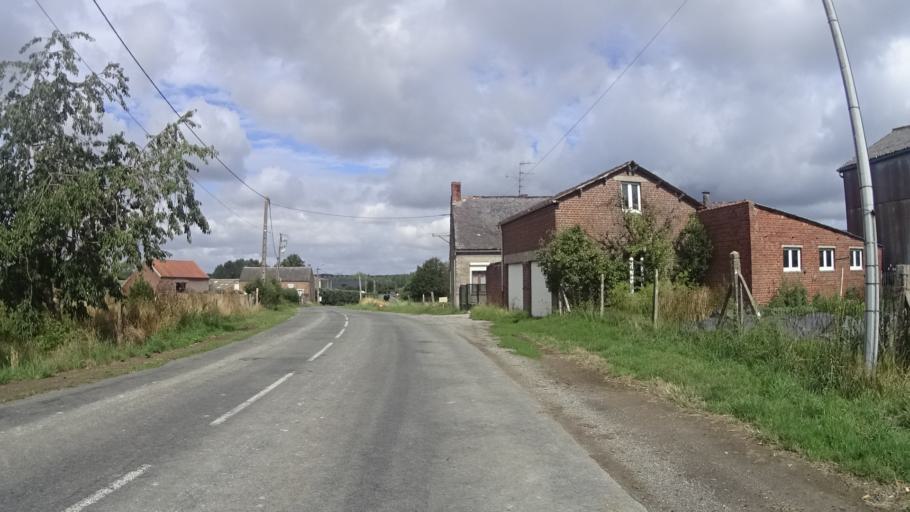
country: FR
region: Nord-Pas-de-Calais
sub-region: Departement du Nord
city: Landrecies
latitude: 50.0902
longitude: 3.6416
